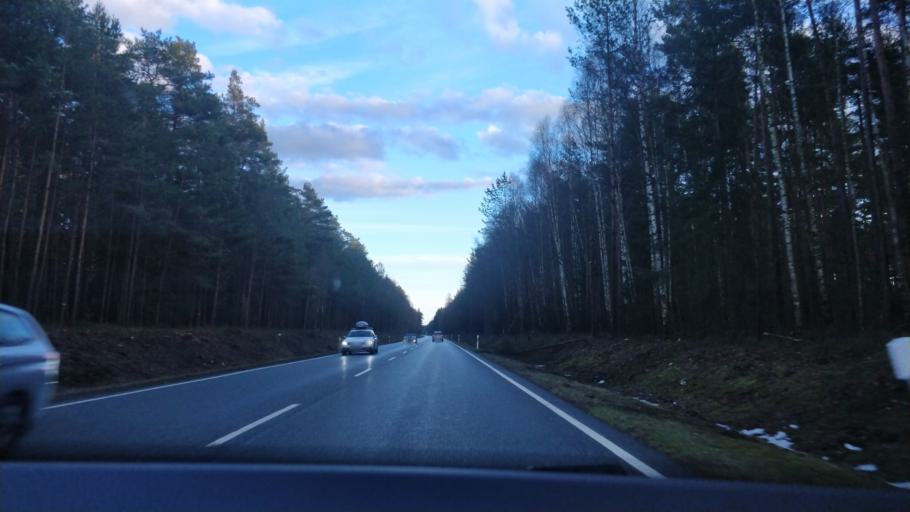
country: DE
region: Bavaria
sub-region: Upper Palatinate
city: Pressath
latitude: 49.7354
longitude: 11.9535
